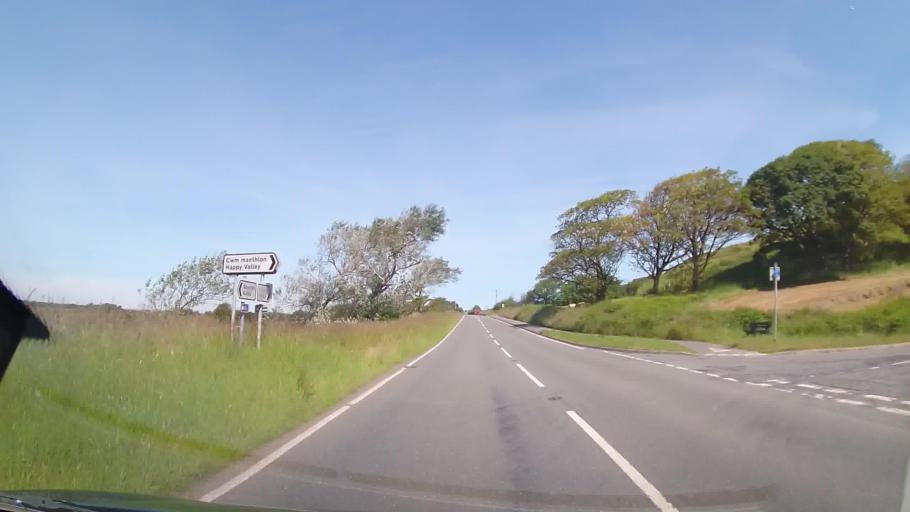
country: GB
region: Wales
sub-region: Gwynedd
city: Tywyn
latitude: 52.5751
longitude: -4.0713
